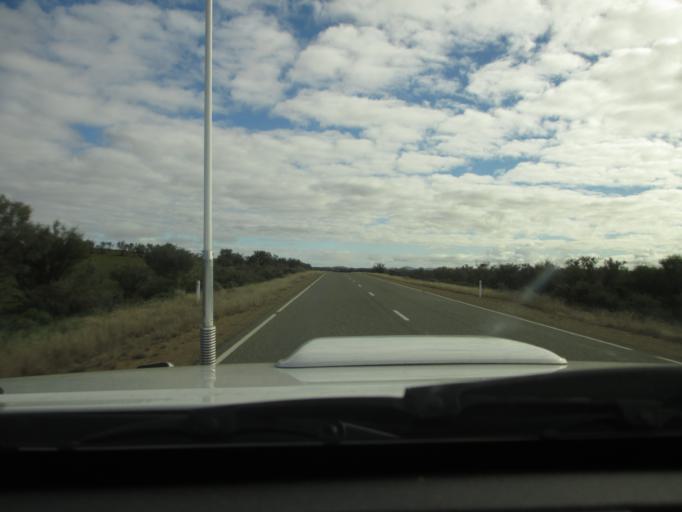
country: AU
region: South Australia
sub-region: Flinders Ranges
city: Quorn
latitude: -32.3948
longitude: 138.5101
